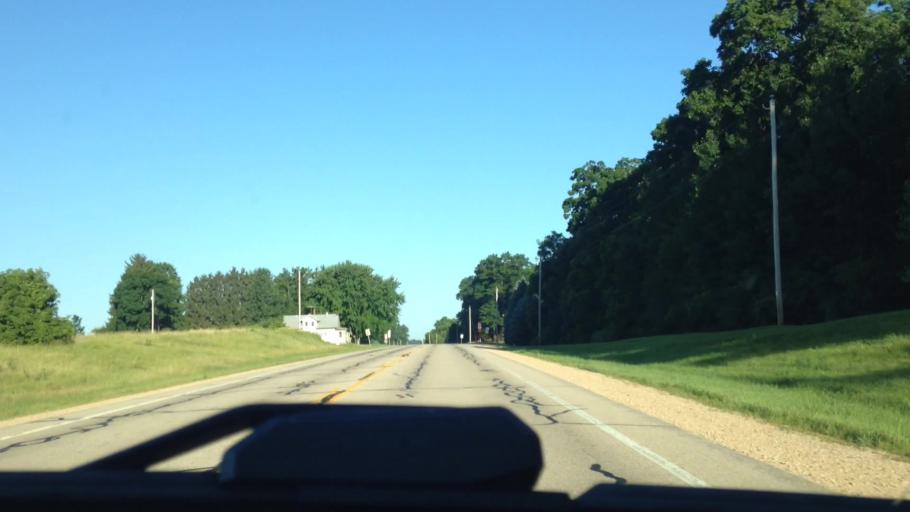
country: US
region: Wisconsin
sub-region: Columbia County
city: Fall River
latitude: 43.3406
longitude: -89.1441
